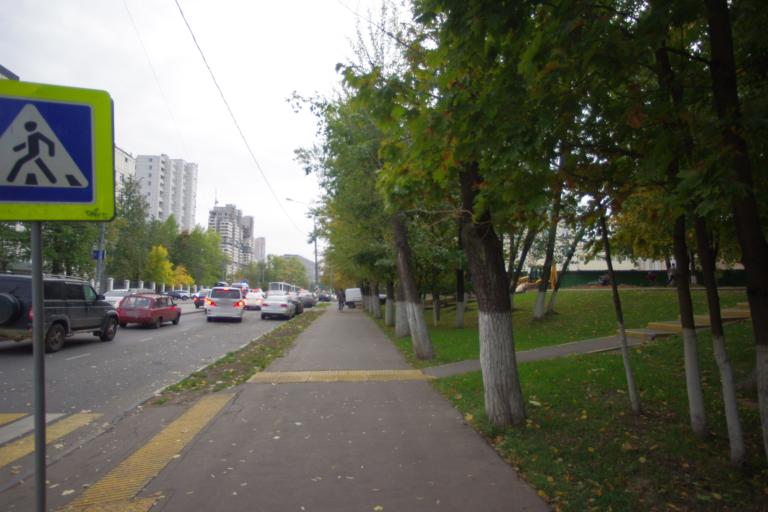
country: RU
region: Moskovskaya
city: Semenovskoye
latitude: 55.6869
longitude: 37.5555
